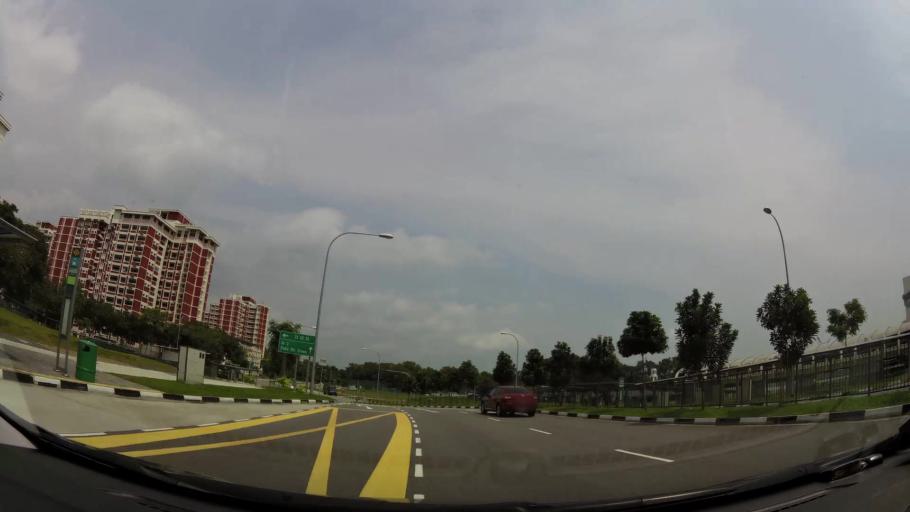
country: MY
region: Johor
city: Kampung Pasir Gudang Baru
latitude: 1.3729
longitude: 103.9477
